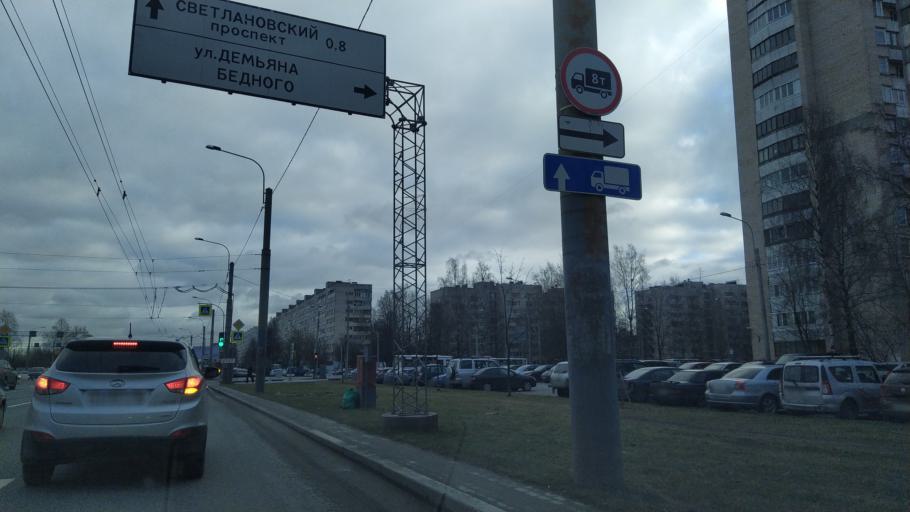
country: RU
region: St.-Petersburg
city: Grazhdanka
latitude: 60.0505
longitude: 30.3914
